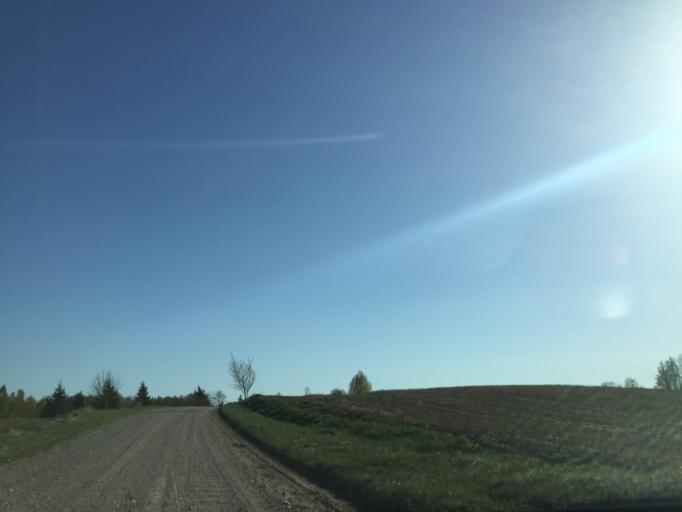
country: LV
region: Ergli
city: Ergli
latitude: 56.8965
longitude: 25.4948
